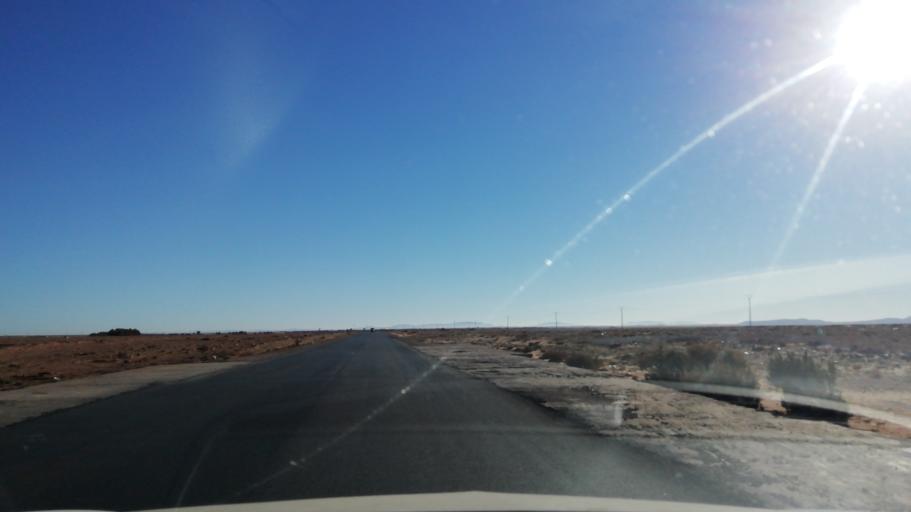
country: DZ
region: El Bayadh
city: El Bayadh
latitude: 33.8557
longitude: 0.5965
